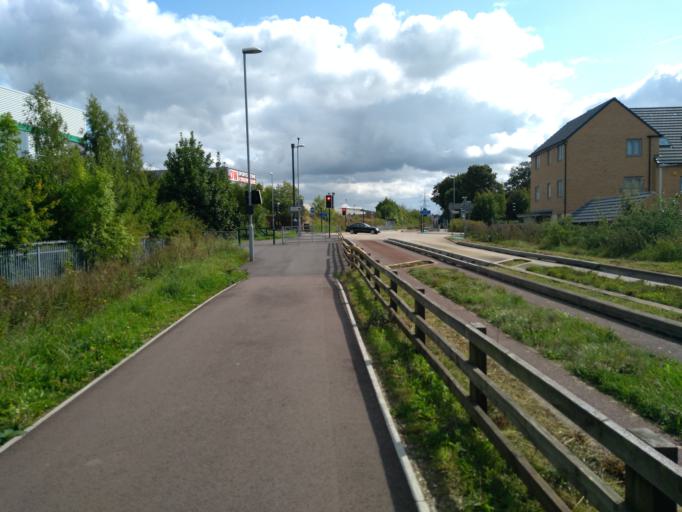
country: GB
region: England
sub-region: Central Bedfordshire
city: Dunstable
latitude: 51.8916
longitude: -0.5164
